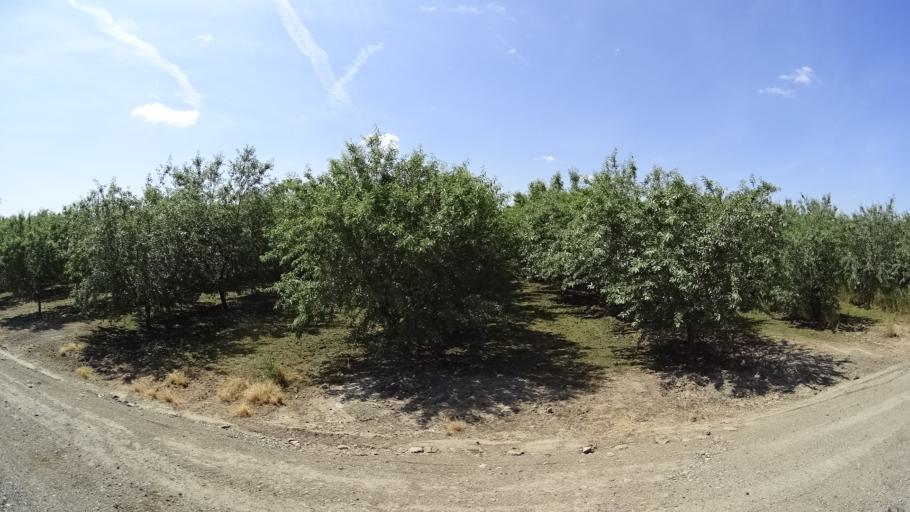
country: US
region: California
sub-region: Kings County
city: Home Garden
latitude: 36.2695
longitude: -119.5710
